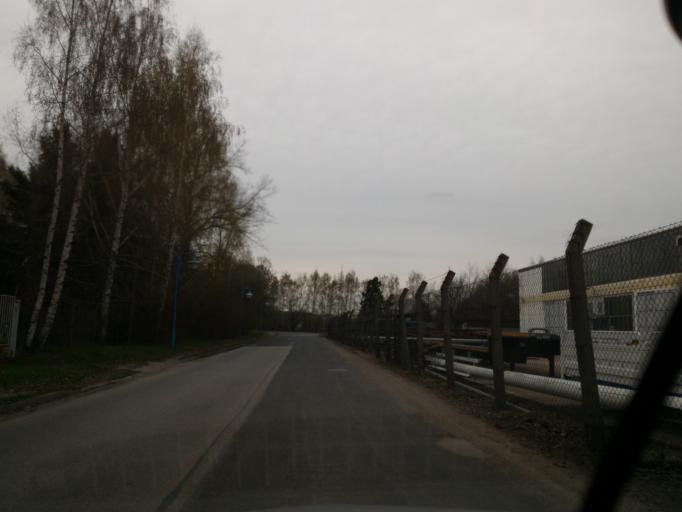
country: DE
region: Saxony
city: Zittau
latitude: 50.8824
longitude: 14.7974
